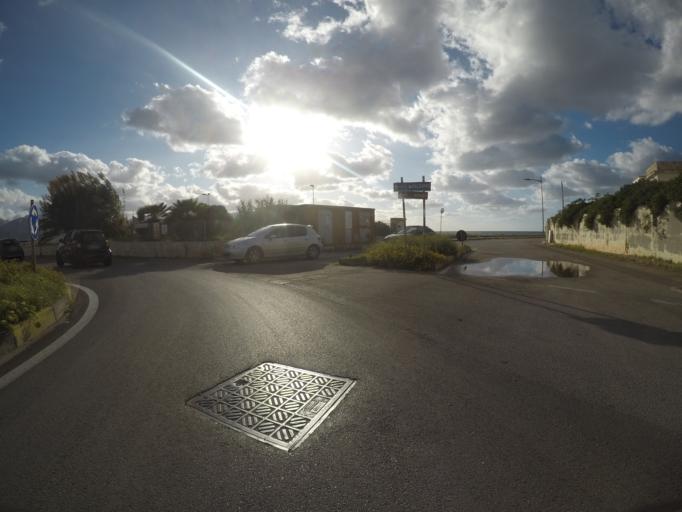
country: IT
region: Sicily
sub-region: Palermo
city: Isola delle Femmine
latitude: 38.1995
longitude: 13.2438
